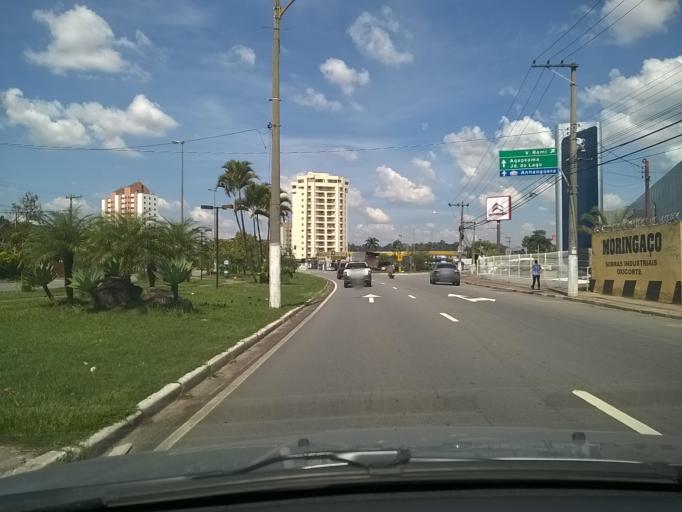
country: BR
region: Sao Paulo
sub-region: Jundiai
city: Jundiai
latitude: -23.2085
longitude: -46.8789
